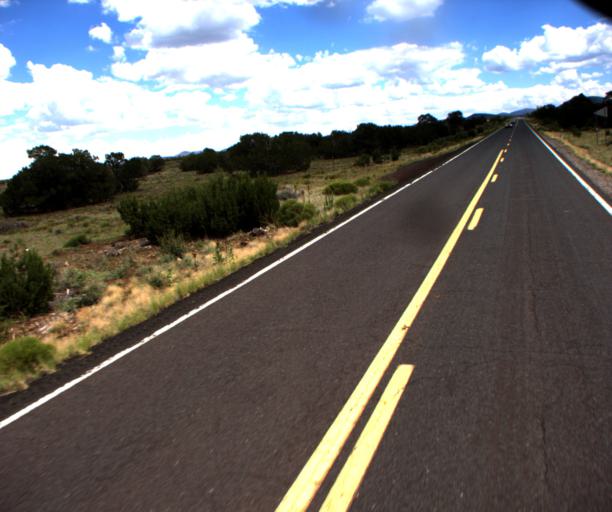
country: US
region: Arizona
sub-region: Coconino County
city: Parks
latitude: 35.5598
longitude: -111.8789
